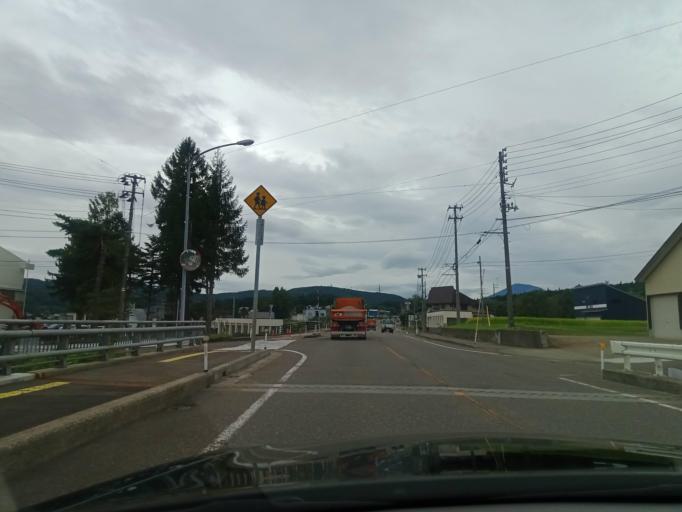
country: JP
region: Niigata
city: Arai
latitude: 36.8831
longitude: 138.2054
